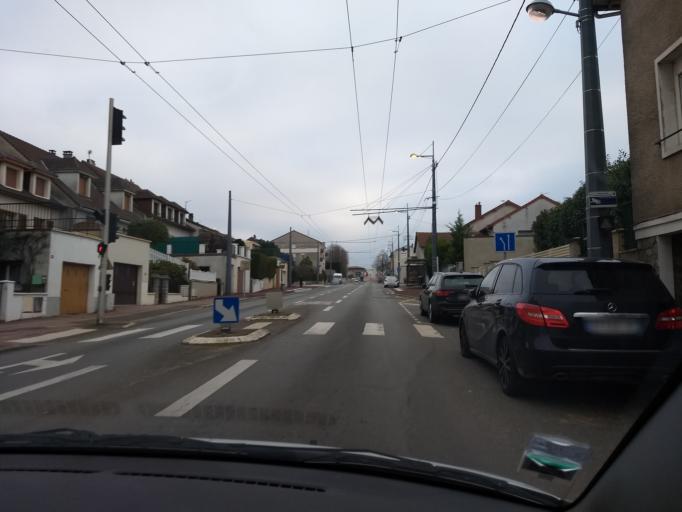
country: FR
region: Limousin
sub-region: Departement de la Haute-Vienne
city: Isle
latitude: 45.8236
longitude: 1.2230
